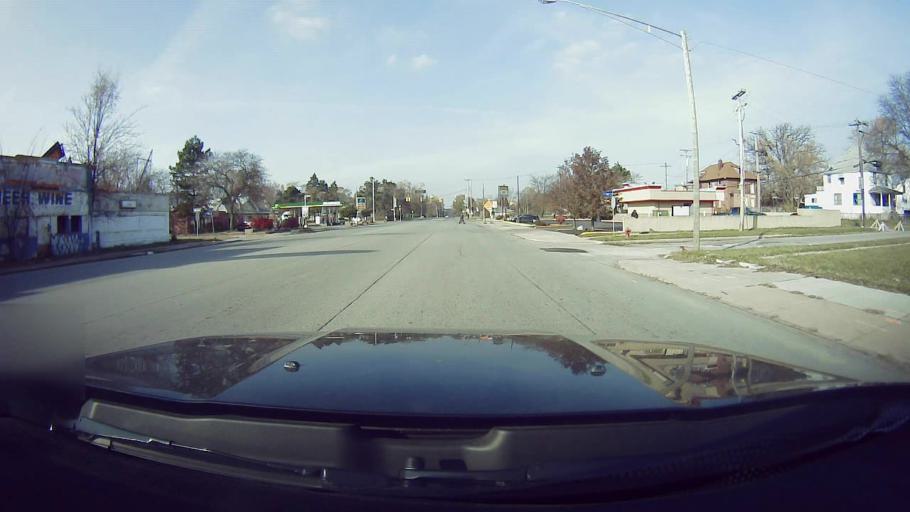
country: US
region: Michigan
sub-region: Wayne County
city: Highland Park
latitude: 42.4167
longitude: -83.1157
